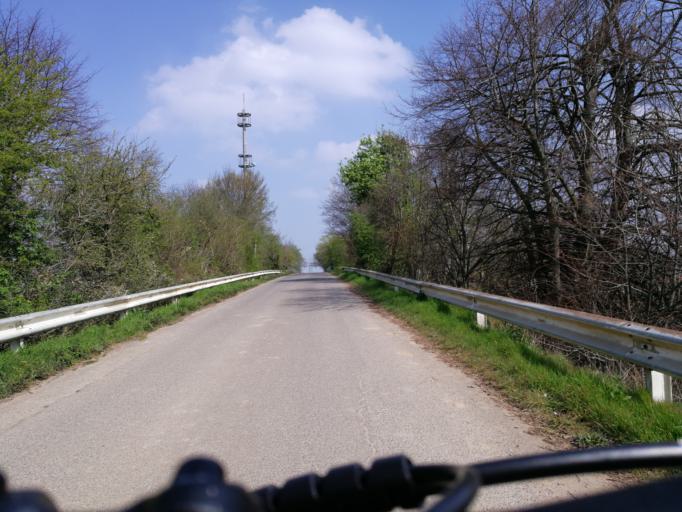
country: DE
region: North Rhine-Westphalia
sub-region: Regierungsbezirk Dusseldorf
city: Dormagen
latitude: 51.1425
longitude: 6.7676
